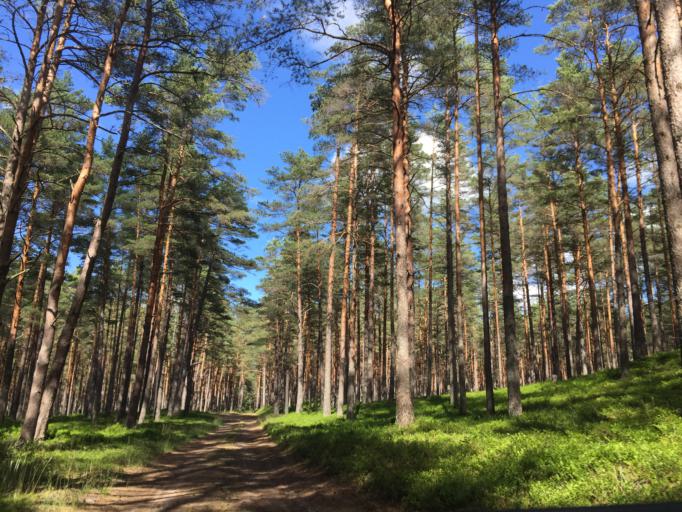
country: LV
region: Ventspils
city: Ventspils
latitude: 57.4679
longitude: 21.6392
